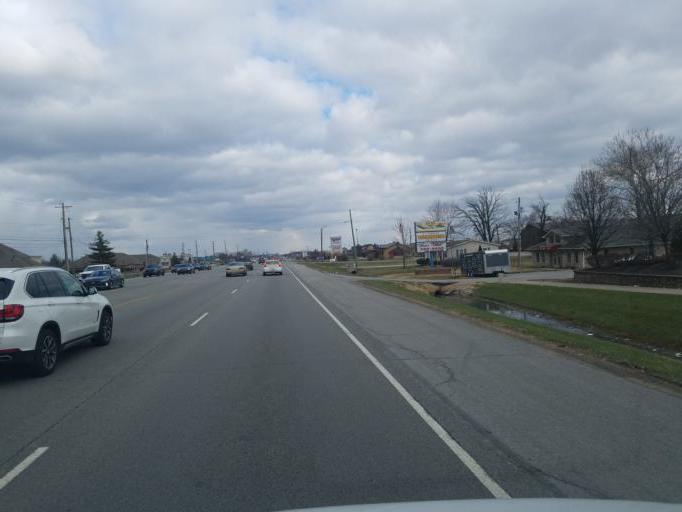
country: US
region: Indiana
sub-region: Marion County
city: Clermont
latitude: 39.7636
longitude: -86.3470
